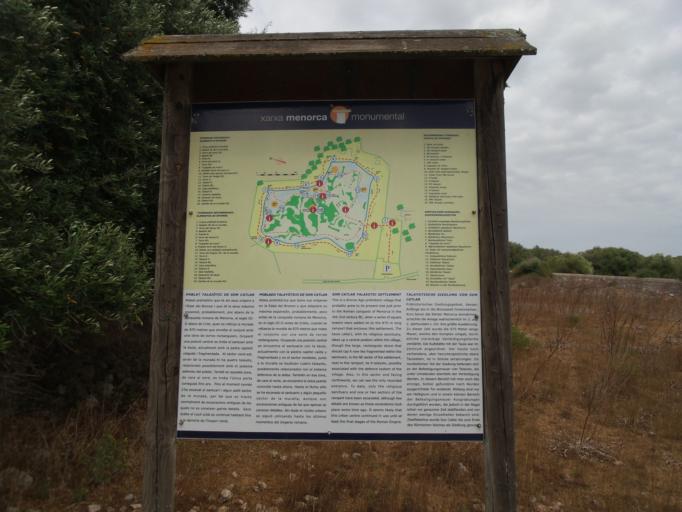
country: ES
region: Balearic Islands
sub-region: Illes Balears
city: Ciutadella
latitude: 39.9527
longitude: 3.8750
